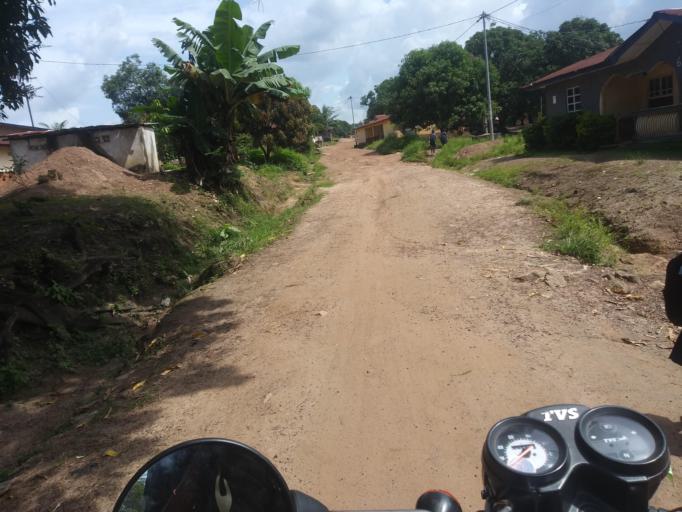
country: SL
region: Northern Province
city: Makeni
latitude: 8.8810
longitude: -12.0355
